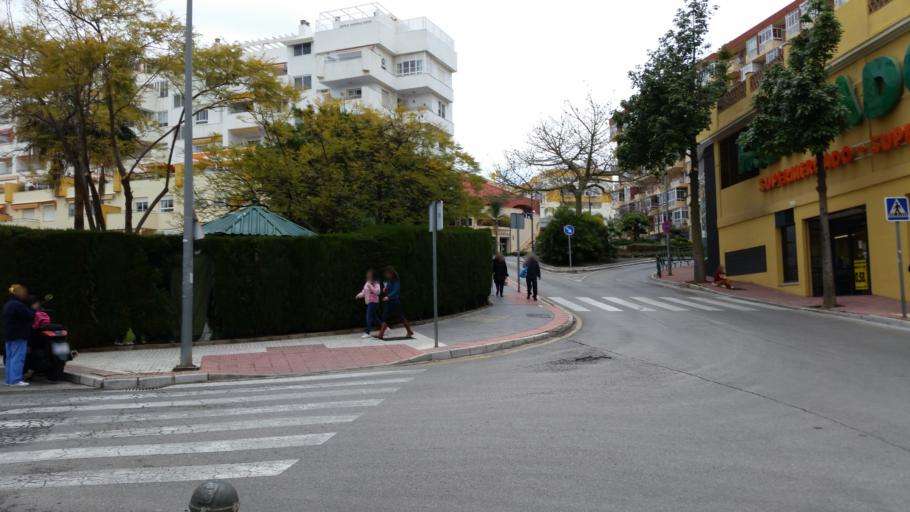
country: ES
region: Andalusia
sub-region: Provincia de Malaga
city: Benalmadena
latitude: 36.5957
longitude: -4.5317
